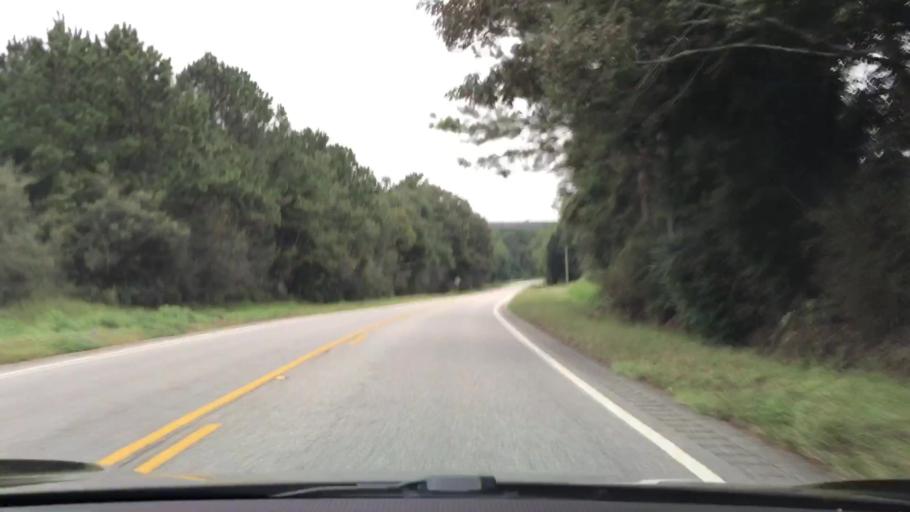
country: US
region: Alabama
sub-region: Covington County
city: Opp
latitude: 31.3059
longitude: -86.1417
